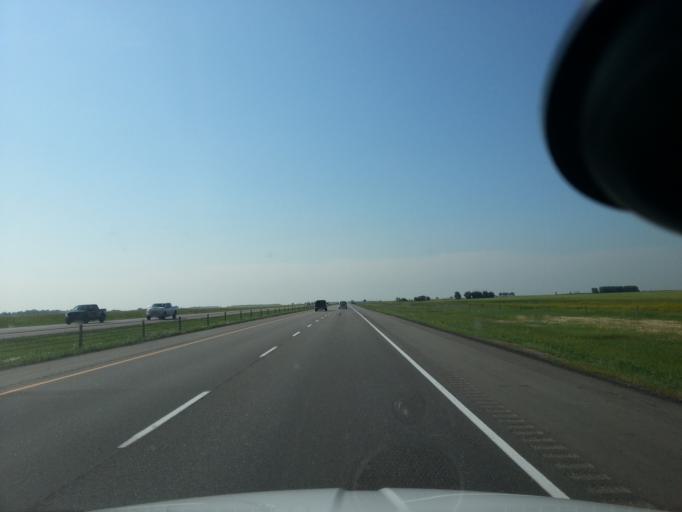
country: CA
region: Alberta
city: Didsbury
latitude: 51.6968
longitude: -114.0256
